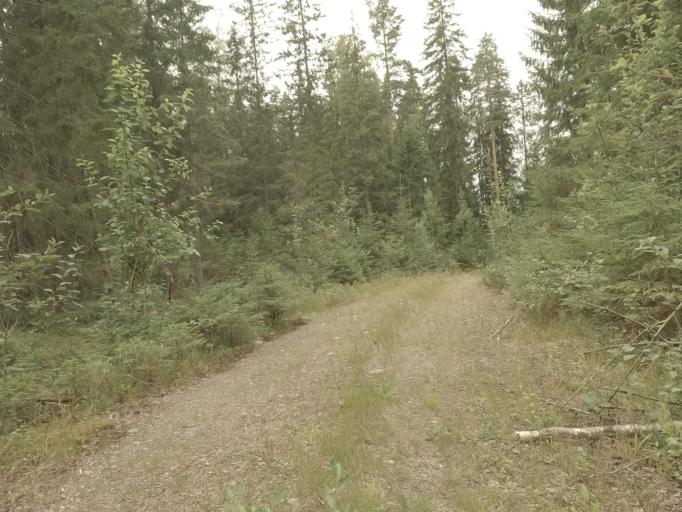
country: RU
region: Leningrad
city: Kamennogorsk
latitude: 61.0210
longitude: 29.1691
